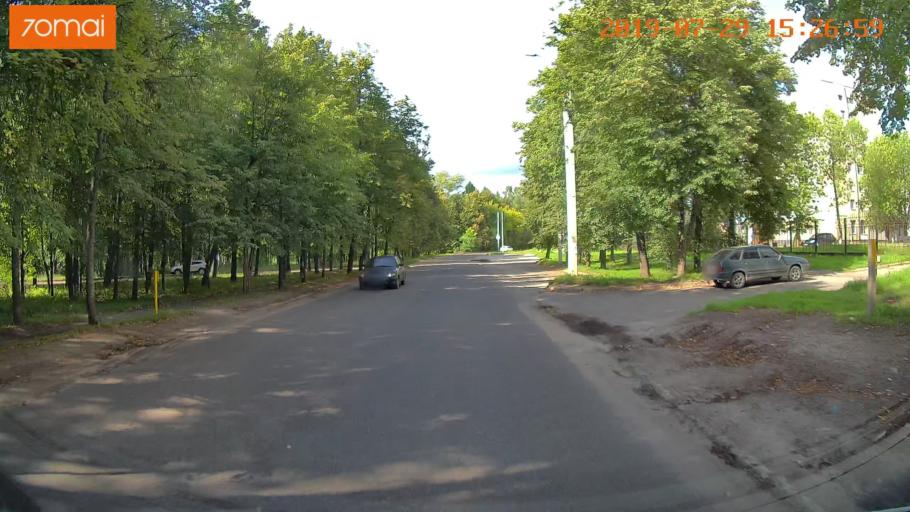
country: RU
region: Ivanovo
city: Bogorodskoye
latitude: 57.0194
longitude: 41.0056
